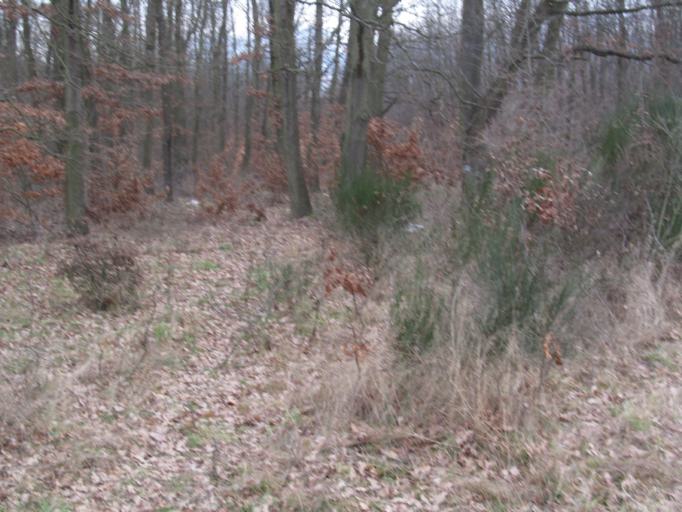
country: HU
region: Vas
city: Sarvar
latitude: 47.2408
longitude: 17.0048
